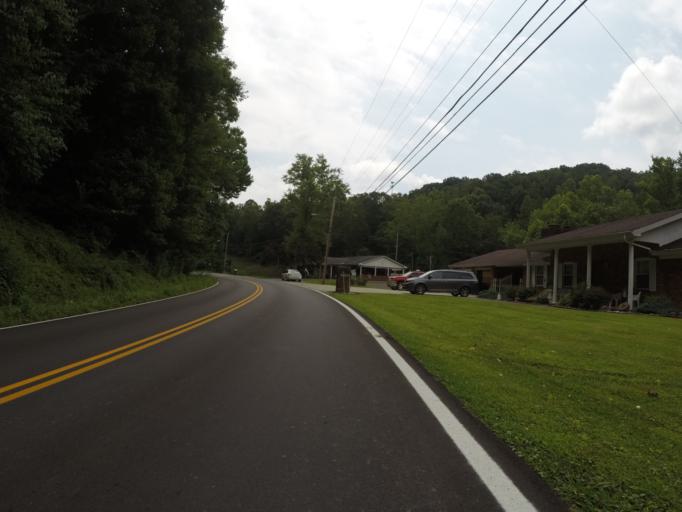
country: US
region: Kentucky
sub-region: Boyd County
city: Ashland
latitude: 38.4372
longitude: -82.6341
